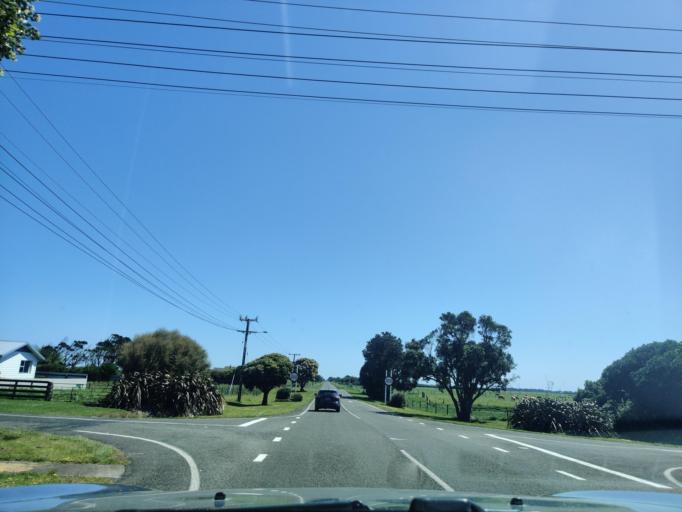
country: NZ
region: Taranaki
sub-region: South Taranaki District
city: Hawera
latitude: -39.5503
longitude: 174.1190
